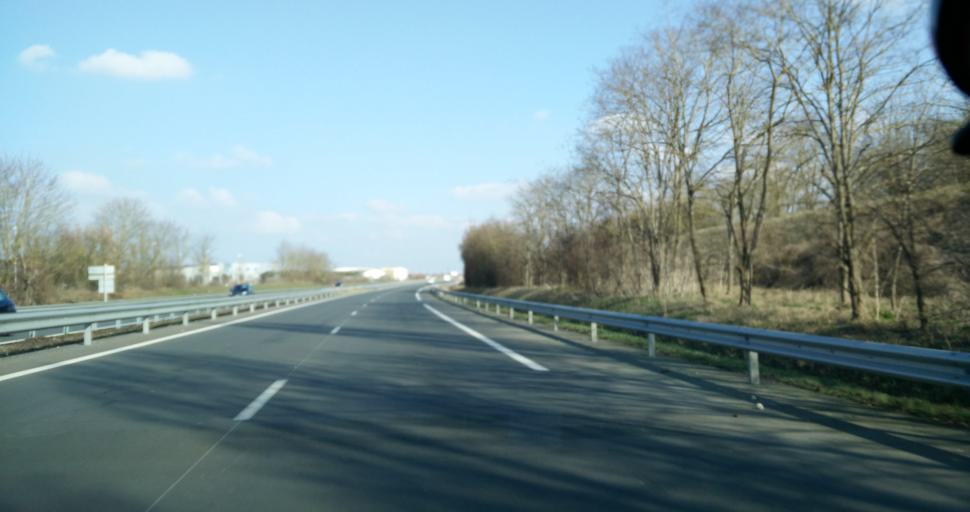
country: FR
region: Poitou-Charentes
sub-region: Departement de la Charente-Maritime
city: Sainte-Soulle
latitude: 46.2050
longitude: -1.0189
